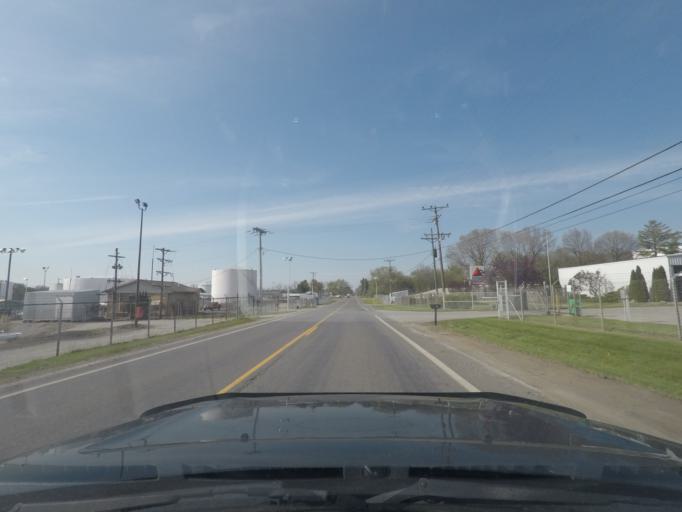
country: US
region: Michigan
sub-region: Berrien County
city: Niles
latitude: 41.7861
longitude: -86.2548
